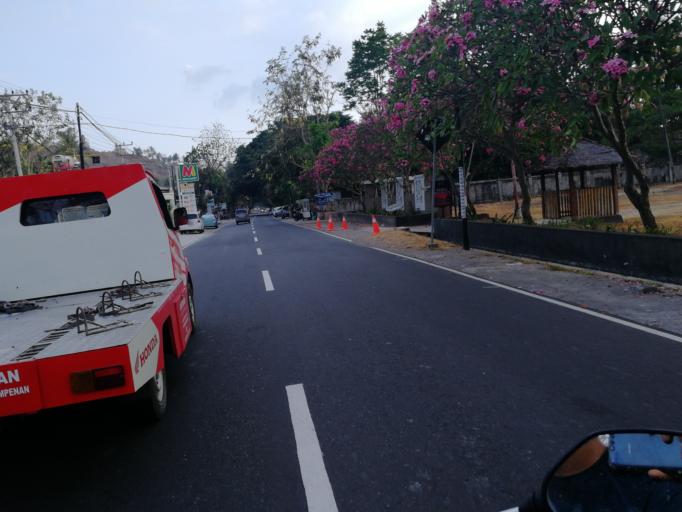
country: ID
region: West Nusa Tenggara
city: Karangsubagan
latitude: -8.4769
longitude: 116.0389
